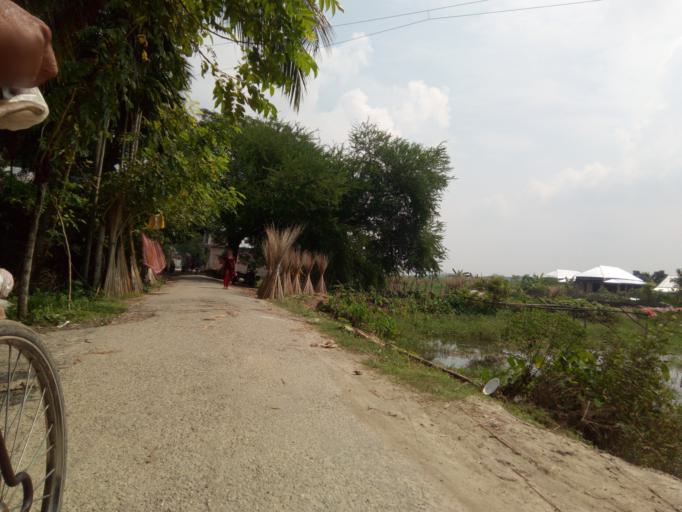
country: BD
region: Khulna
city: Kalia
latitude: 23.0815
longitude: 89.6679
